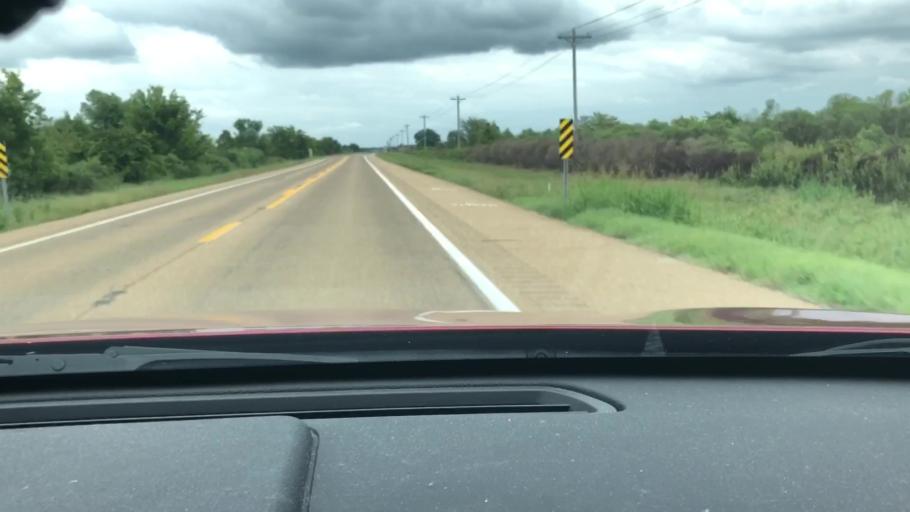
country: US
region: Arkansas
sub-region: Lafayette County
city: Lewisville
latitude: 33.4127
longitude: -93.8019
